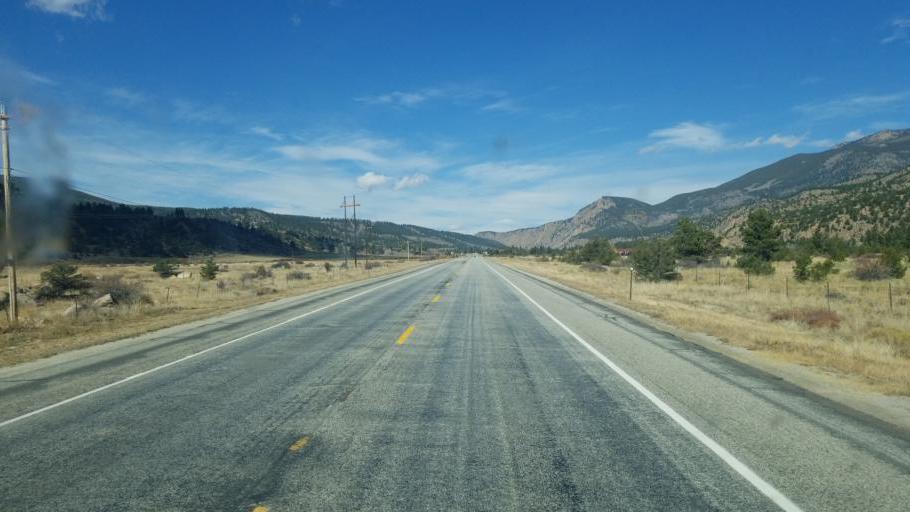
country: US
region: Colorado
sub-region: Chaffee County
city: Buena Vista
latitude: 38.9496
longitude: -106.1957
